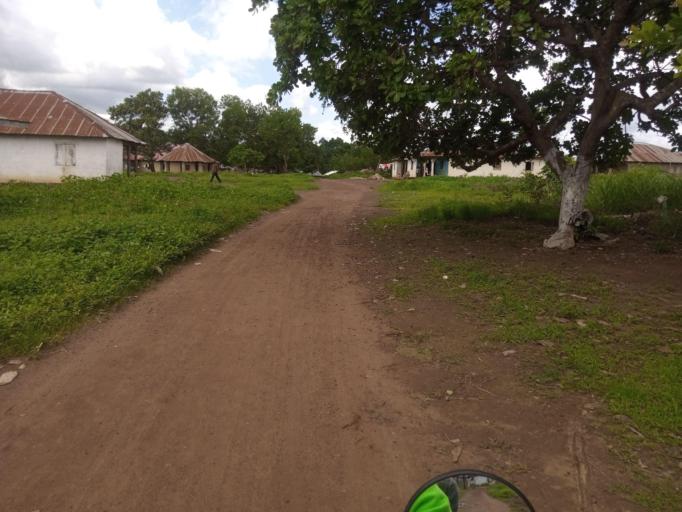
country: SL
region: Northern Province
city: Port Loko
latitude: 8.7776
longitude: -12.7711
